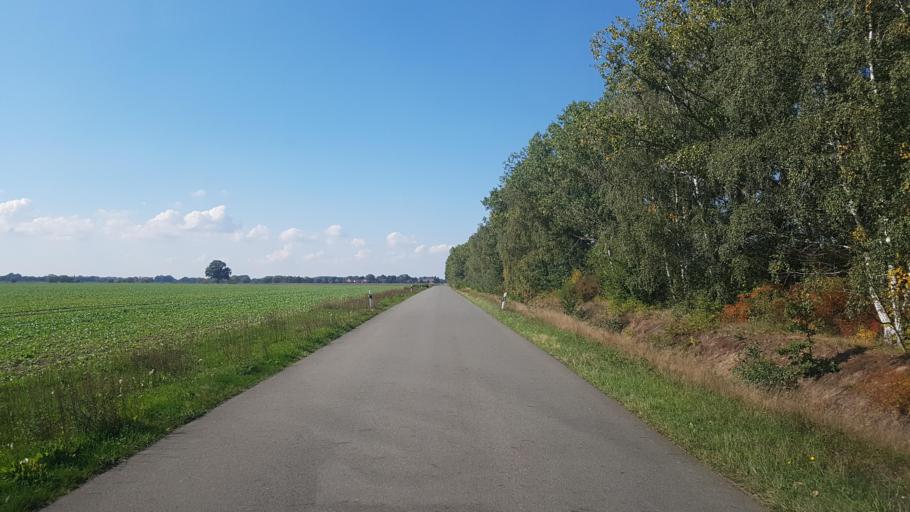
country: DE
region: Brandenburg
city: Dahme
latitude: 51.8311
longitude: 13.3831
